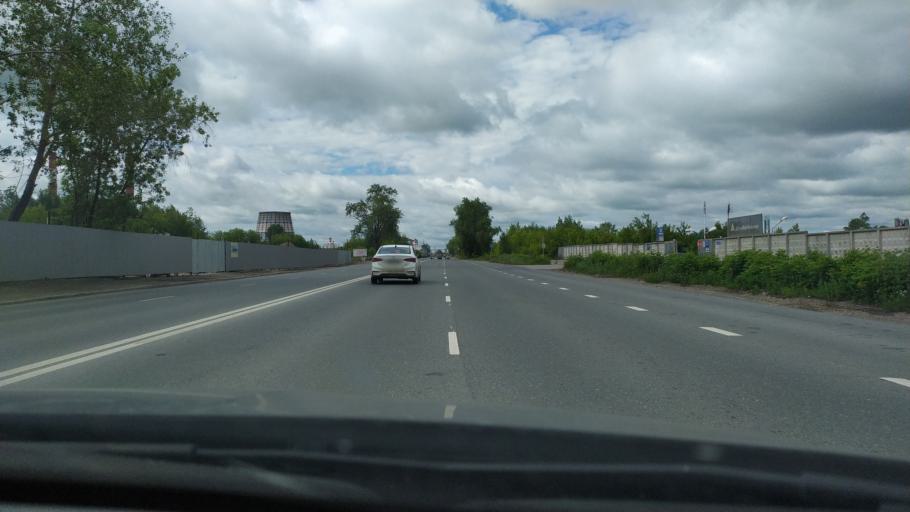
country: RU
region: Perm
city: Kondratovo
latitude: 57.9326
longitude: 56.1508
